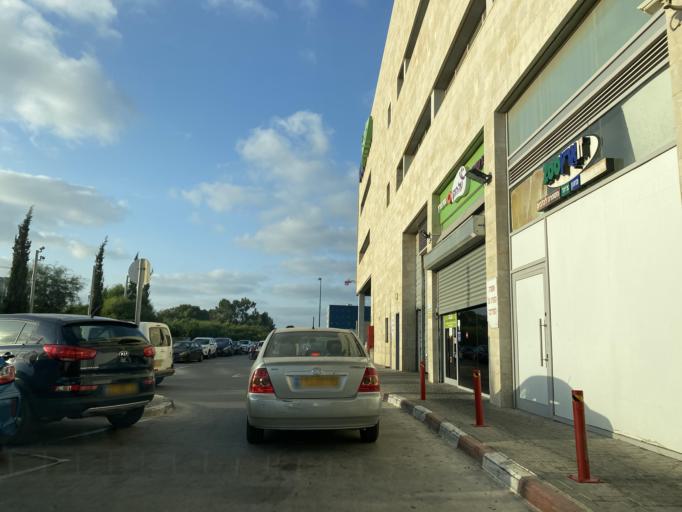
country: IL
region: Central District
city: Netanya
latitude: 32.3072
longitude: 34.8688
